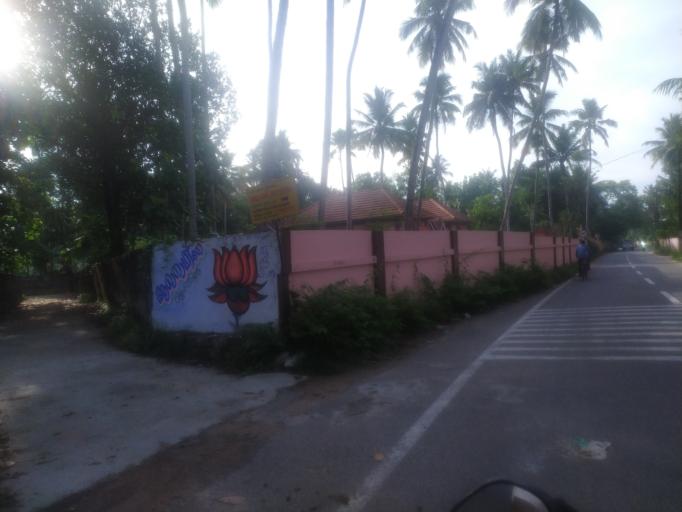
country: IN
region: Kerala
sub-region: Thiruvananthapuram
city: Attingal
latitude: 8.6175
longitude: 76.8276
